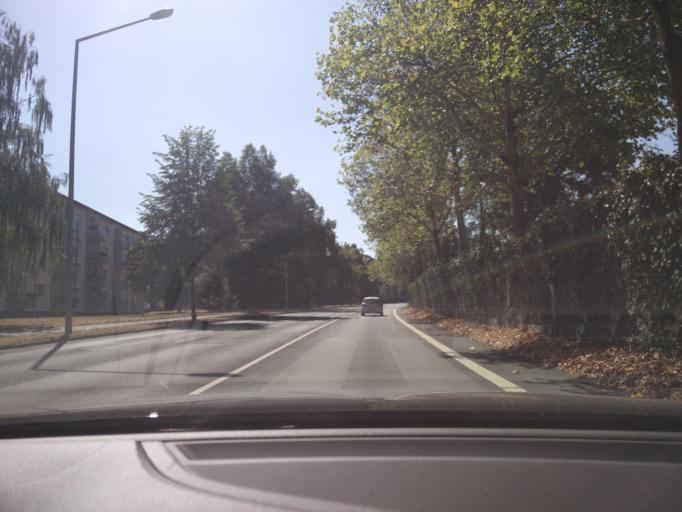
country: DE
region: North Rhine-Westphalia
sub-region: Regierungsbezirk Detmold
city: Paderborn
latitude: 51.7237
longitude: 8.7777
